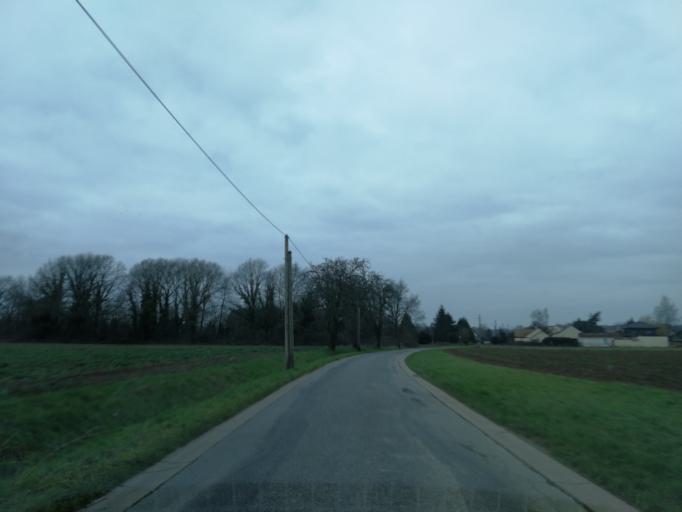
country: FR
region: Ile-de-France
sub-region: Departement de l'Essonne
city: Les Molieres
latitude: 48.6682
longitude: 2.0732
